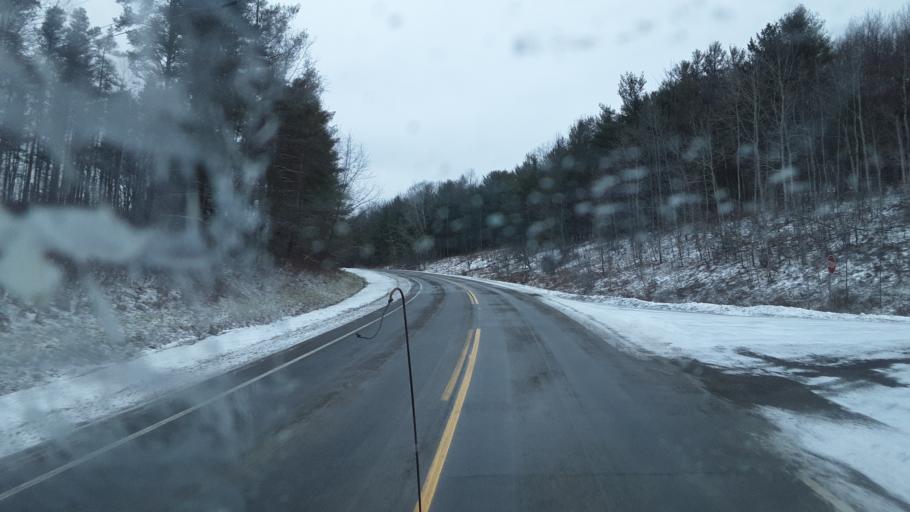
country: US
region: New York
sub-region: Allegany County
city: Friendship
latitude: 42.2203
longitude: -78.1424
